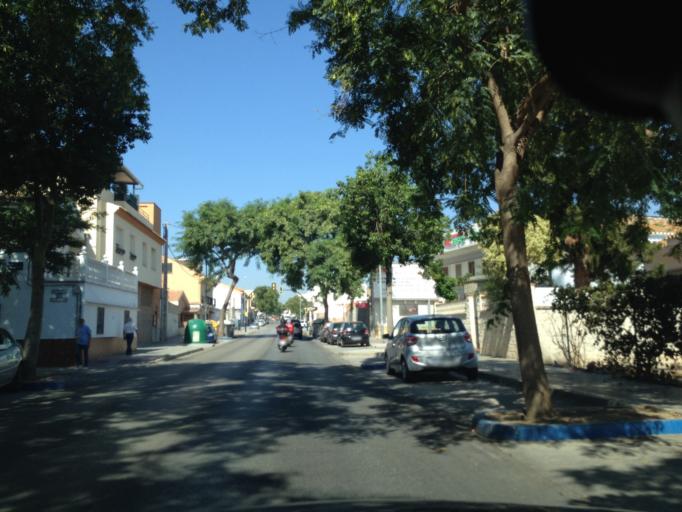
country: ES
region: Andalusia
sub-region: Provincia de Malaga
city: Alhaurin de la Torre
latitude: 36.7252
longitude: -4.5406
